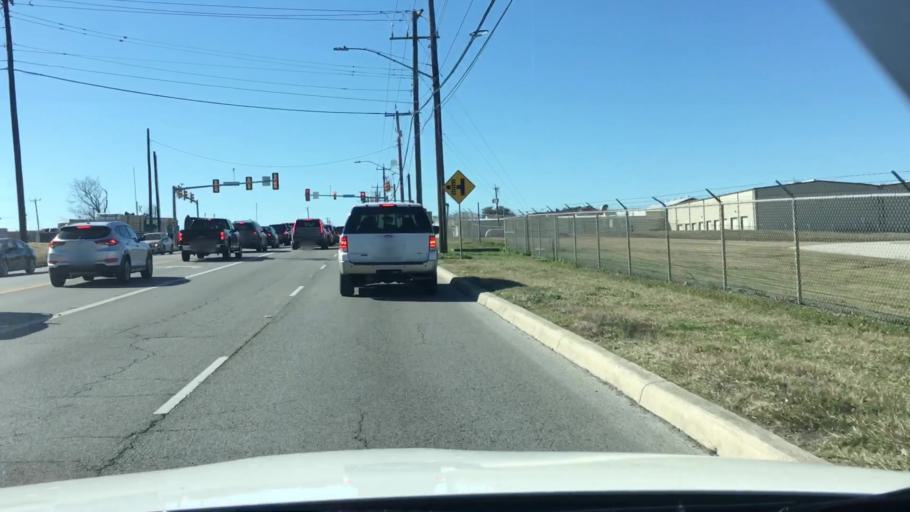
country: US
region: Texas
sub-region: Bexar County
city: Alamo Heights
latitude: 29.5382
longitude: -98.4482
